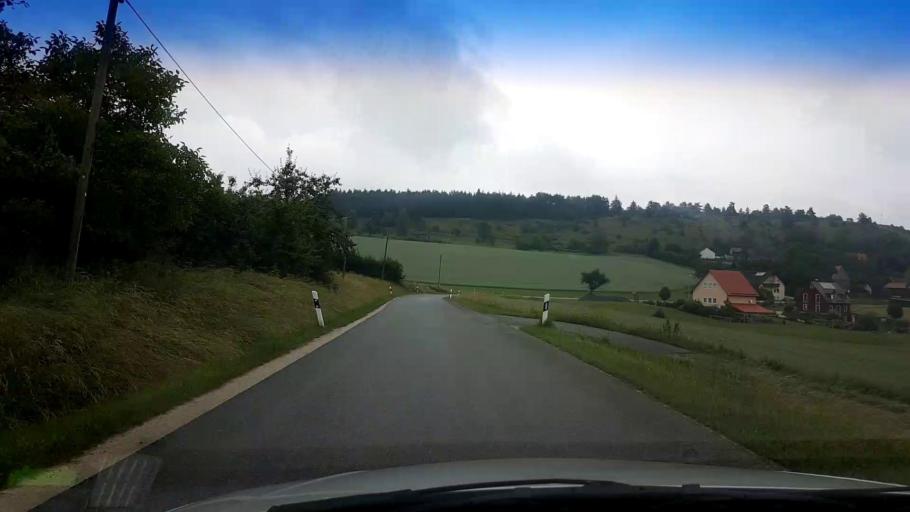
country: DE
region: Bavaria
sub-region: Upper Franconia
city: Altendorf
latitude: 50.0725
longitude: 11.1600
